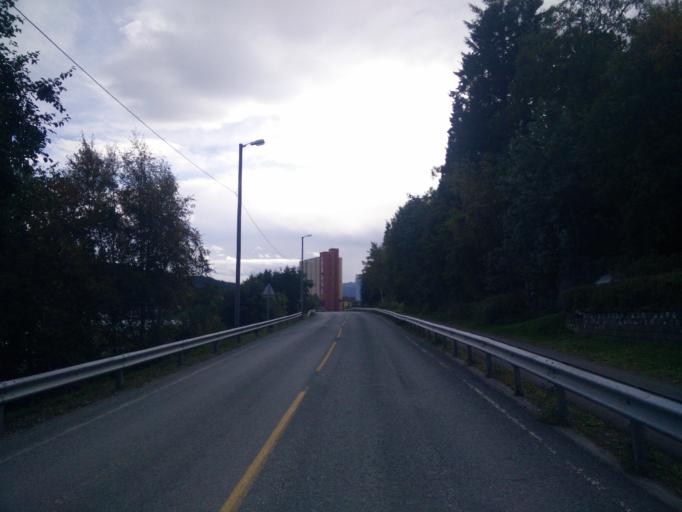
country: NO
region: Sor-Trondelag
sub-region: Skaun
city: Borsa
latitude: 63.3145
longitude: 10.1541
